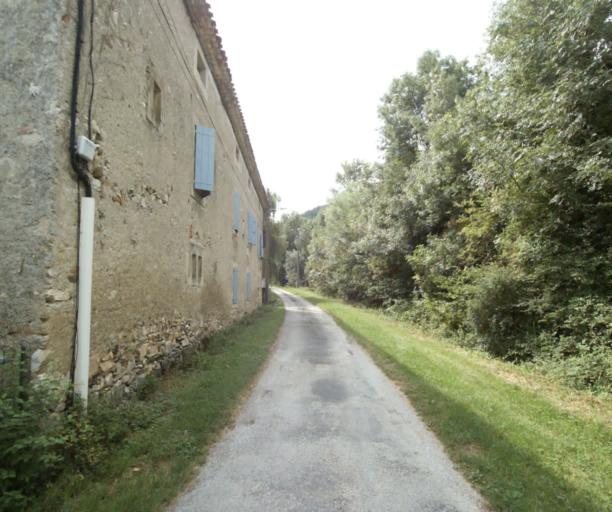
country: FR
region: Midi-Pyrenees
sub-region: Departement du Tarn
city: Soreze
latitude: 43.4647
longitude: 2.1004
